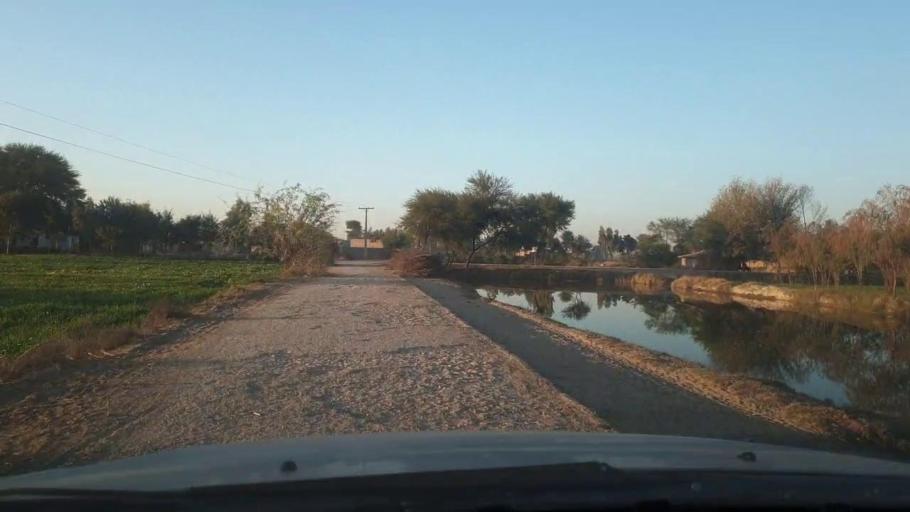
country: PK
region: Sindh
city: Pano Aqil
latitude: 27.9069
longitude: 69.1971
